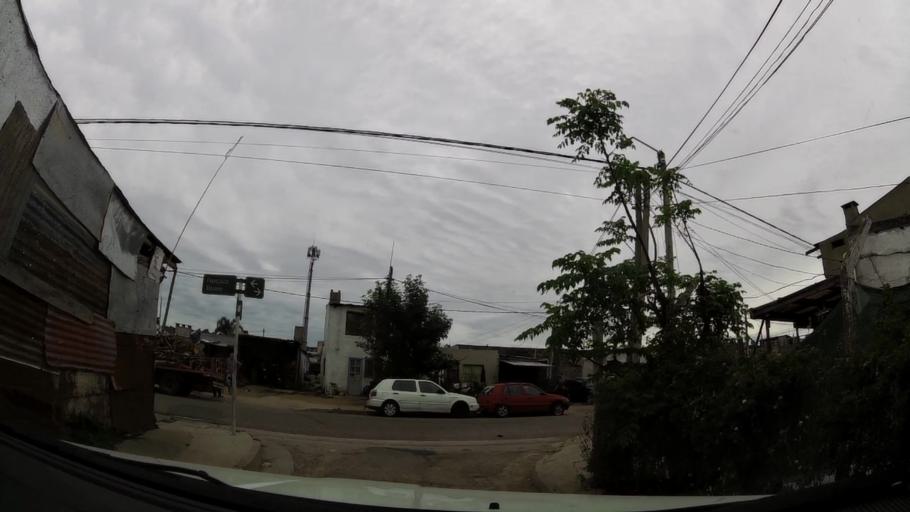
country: UY
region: Maldonado
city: Maldonado
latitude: -34.8946
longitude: -54.9362
